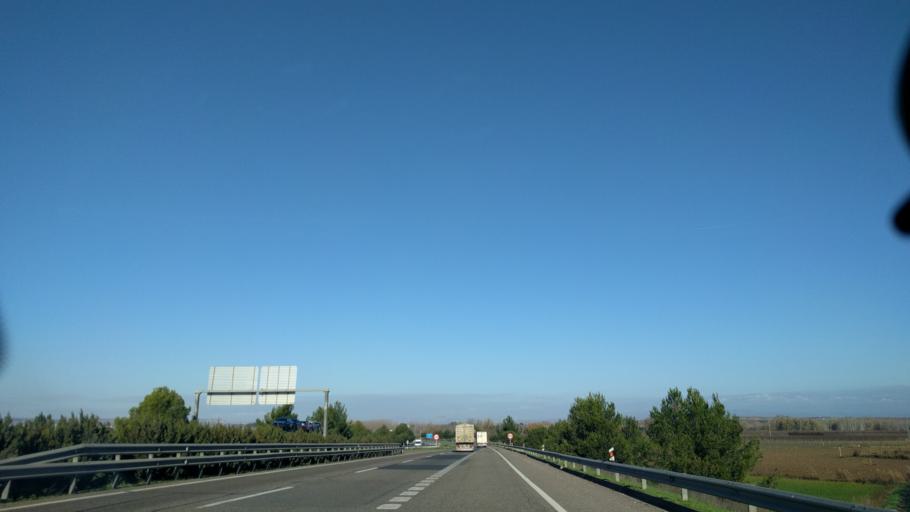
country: ES
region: Catalonia
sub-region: Provincia de Lleida
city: Alcoletge
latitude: 41.6461
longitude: 0.6726
